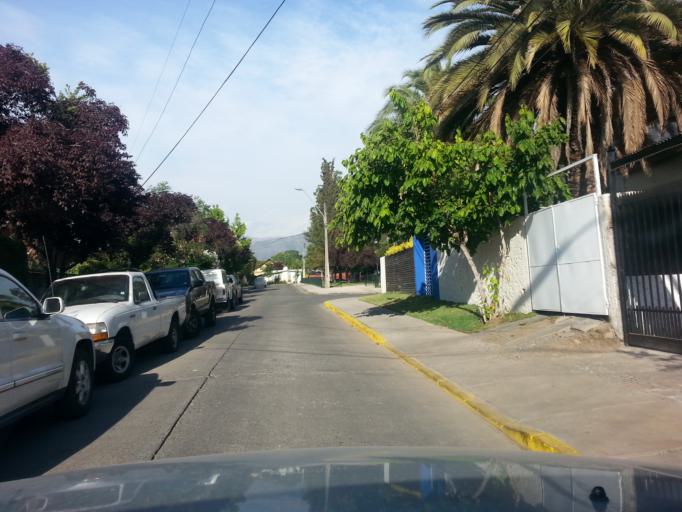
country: CL
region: Santiago Metropolitan
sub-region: Provincia de Santiago
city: Villa Presidente Frei, Nunoa, Santiago, Chile
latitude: -33.3865
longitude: -70.5487
